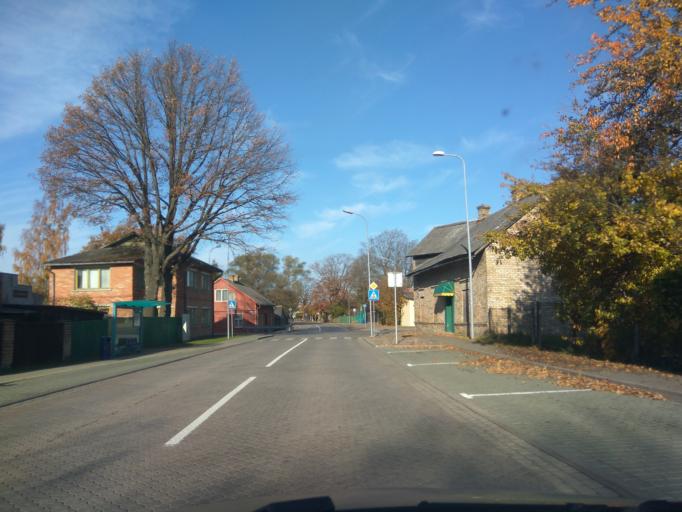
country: LV
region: Ventspils
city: Ventspils
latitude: 57.3760
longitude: 21.5733
